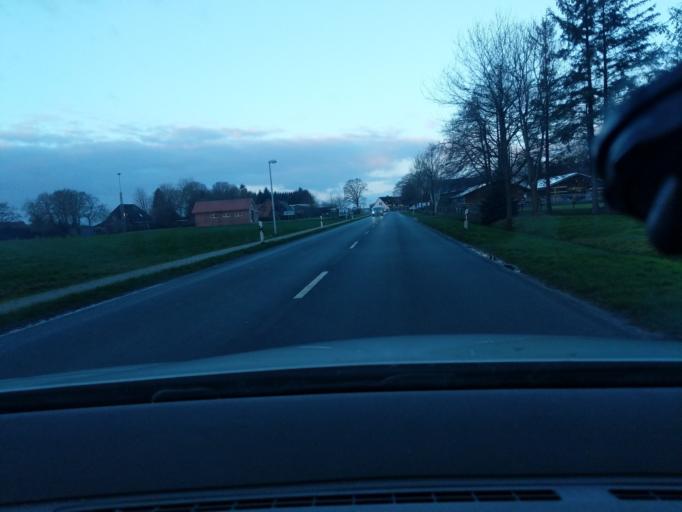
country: DE
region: Lower Saxony
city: Stinstedt
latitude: 53.6349
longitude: 8.9634
